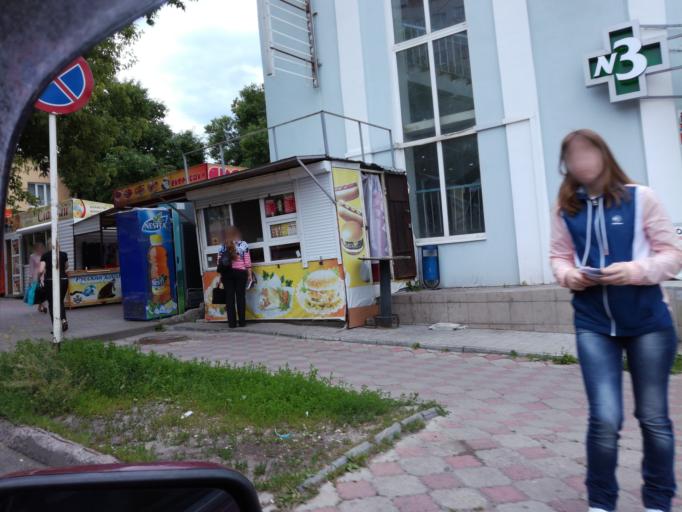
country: RU
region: Kursk
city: Kursk
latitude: 51.7420
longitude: 36.1872
